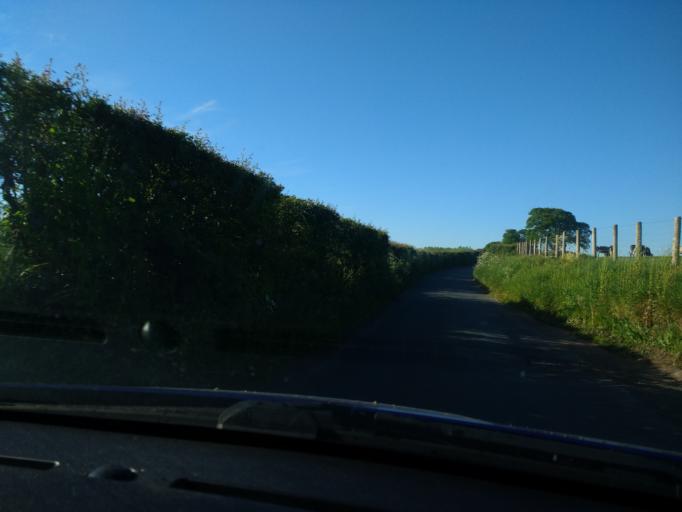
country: GB
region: England
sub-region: Cumbria
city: Appleby-in-Westmorland
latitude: 54.6762
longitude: -2.5902
